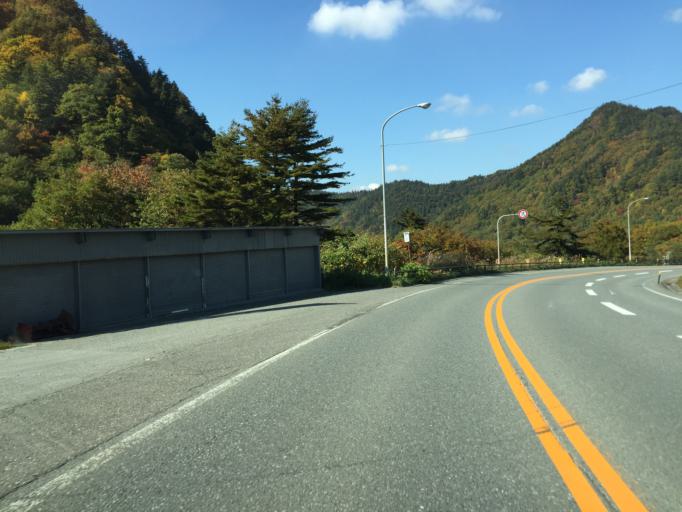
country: JP
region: Yamagata
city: Yonezawa
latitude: 37.8640
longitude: 140.2310
